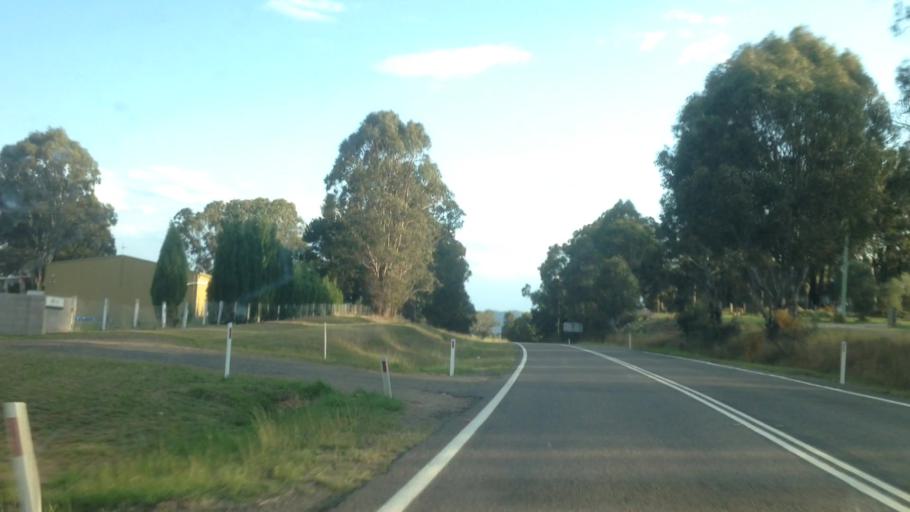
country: AU
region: New South Wales
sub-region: Cessnock
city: Kurri Kurri
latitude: -32.8656
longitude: 151.4801
